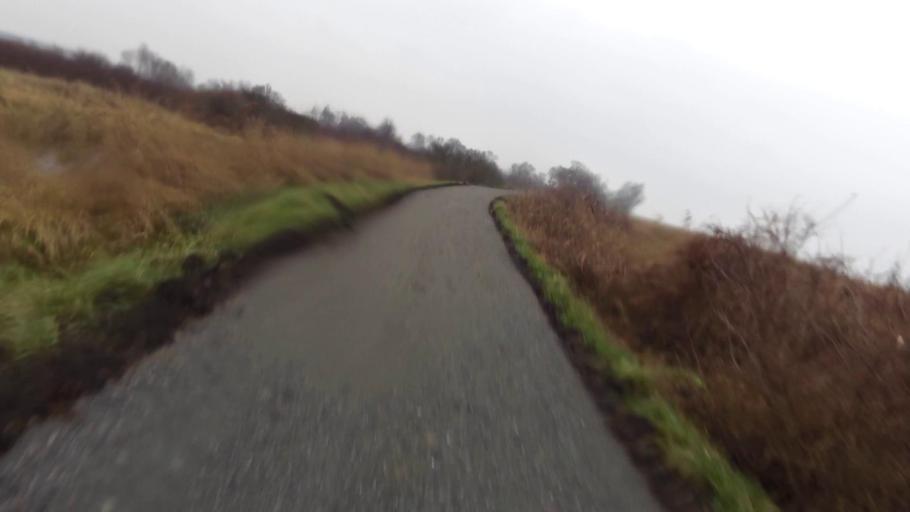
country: PL
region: West Pomeranian Voivodeship
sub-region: Powiat policki
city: Police
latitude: 53.4909
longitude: 14.6948
